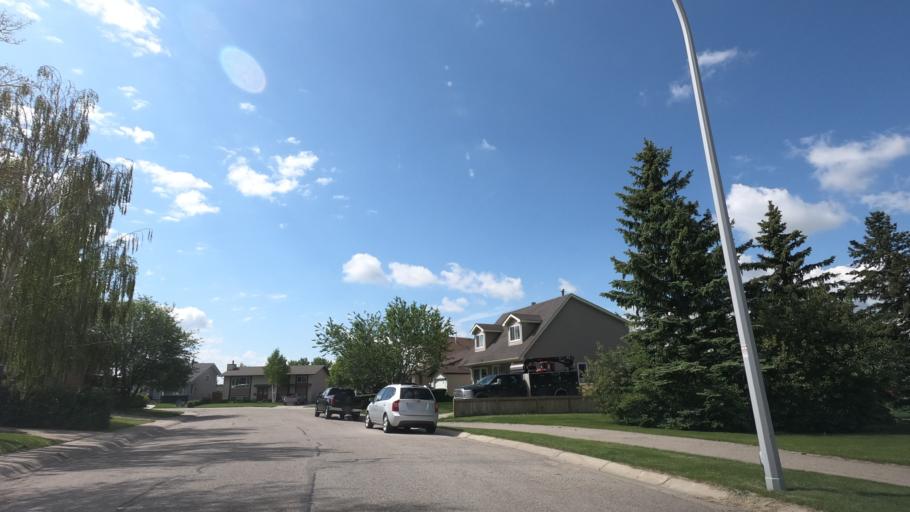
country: CA
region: Alberta
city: Airdrie
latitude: 51.2841
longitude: -114.0152
